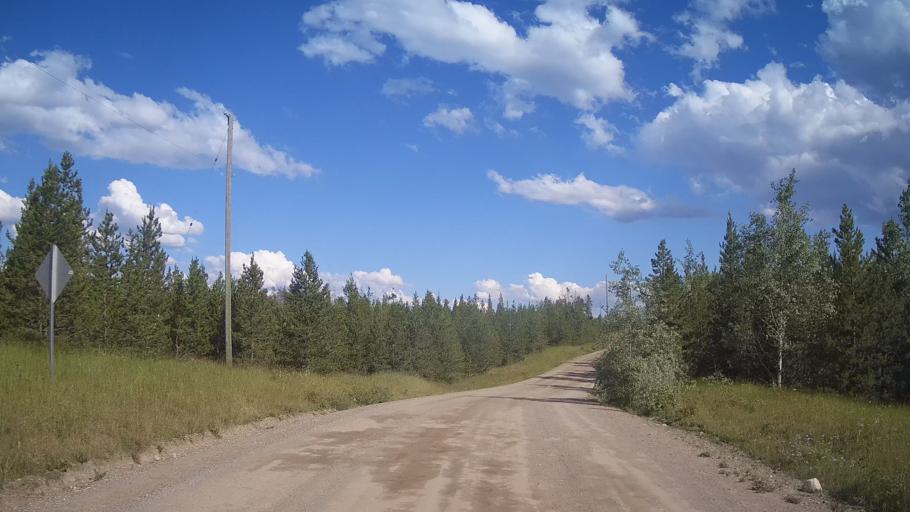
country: CA
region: British Columbia
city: Cache Creek
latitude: 51.2819
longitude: -121.7386
